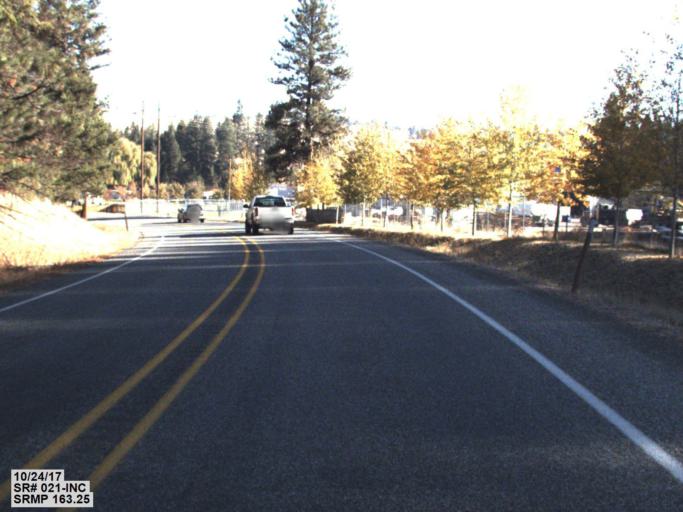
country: US
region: Washington
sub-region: Ferry County
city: Republic
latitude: 48.6506
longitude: -118.6733
